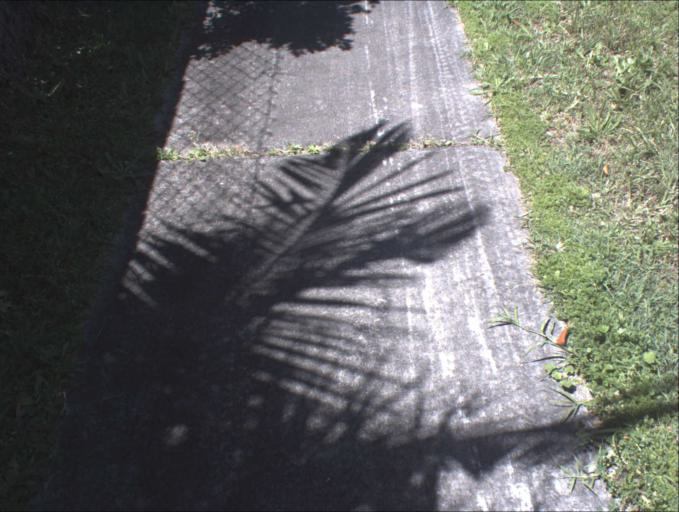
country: AU
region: Queensland
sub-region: Logan
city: Waterford West
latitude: -27.7058
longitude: 153.1658
